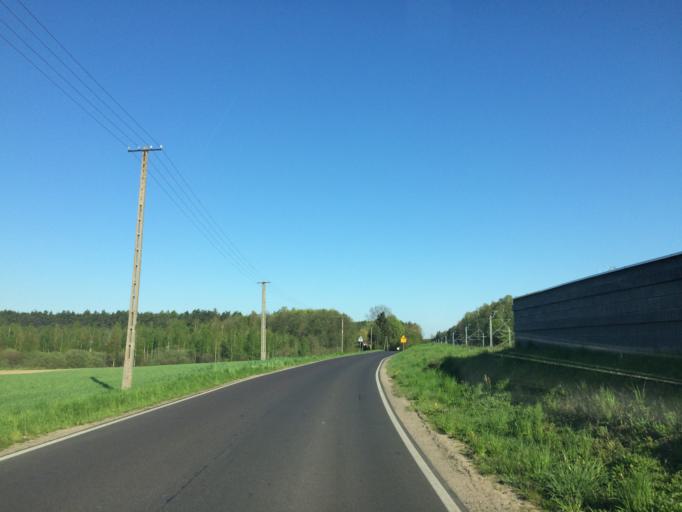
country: PL
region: Warmian-Masurian Voivodeship
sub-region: Powiat dzialdowski
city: Rybno
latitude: 53.4022
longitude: 19.8370
